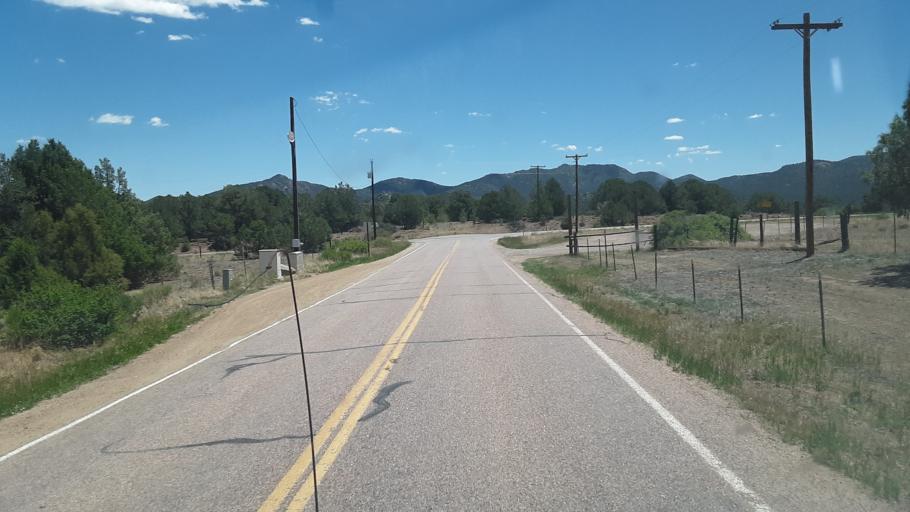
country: US
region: Colorado
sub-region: Custer County
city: Westcliffe
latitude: 38.3093
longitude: -105.6213
